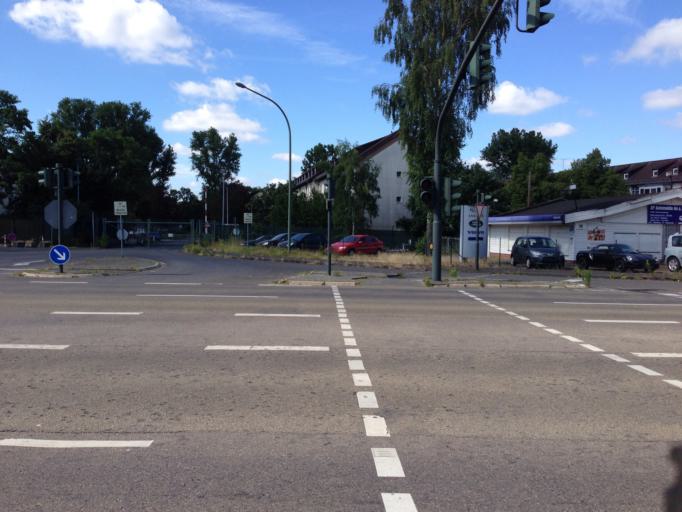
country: DE
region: Hesse
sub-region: Regierungsbezirk Darmstadt
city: Hanau am Main
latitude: 50.1243
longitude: 8.9500
